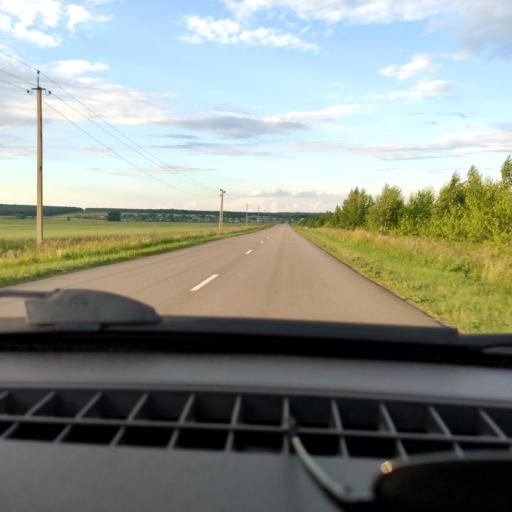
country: RU
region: Bashkortostan
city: Chishmy
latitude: 54.3849
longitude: 55.4397
